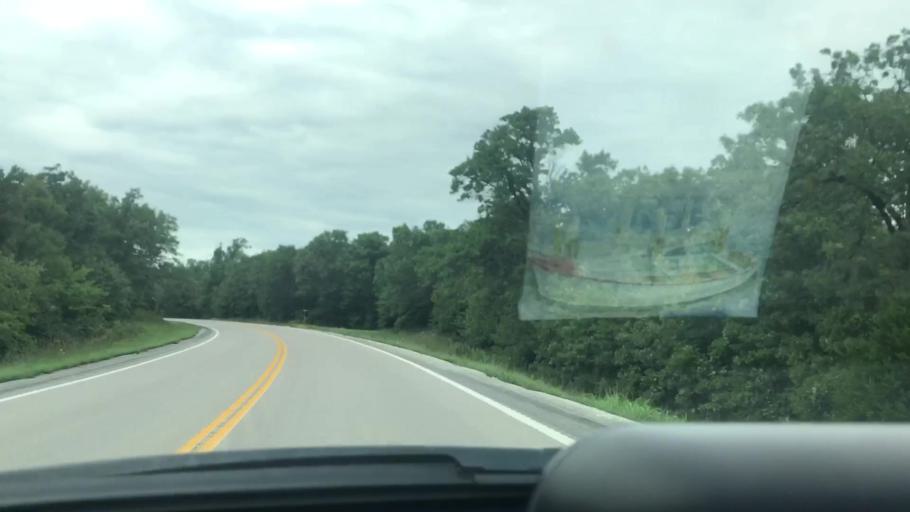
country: US
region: Missouri
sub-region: Benton County
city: Warsaw
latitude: 38.1599
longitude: -93.2979
